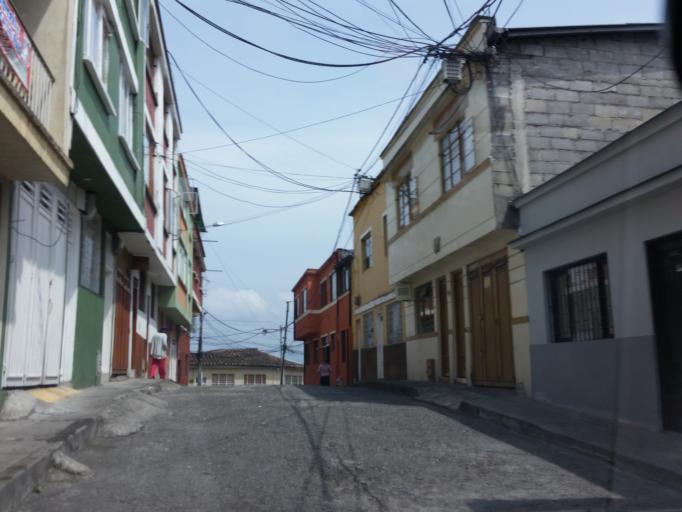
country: CO
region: Caldas
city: Manizales
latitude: 5.0738
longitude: -75.5241
